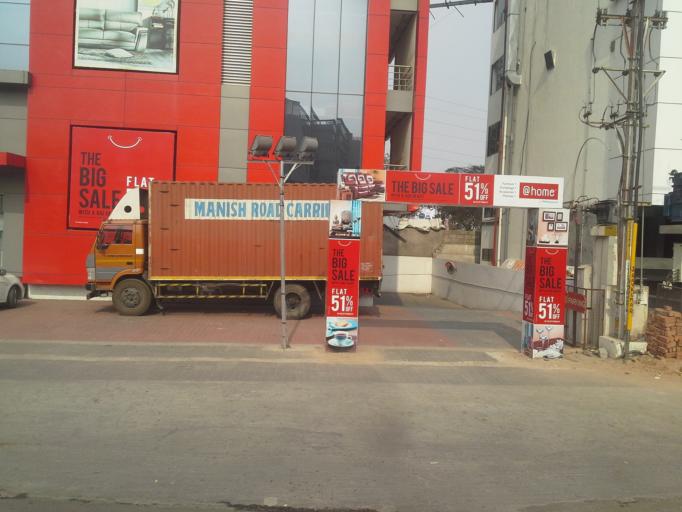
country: IN
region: Telangana
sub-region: Rangareddi
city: Kukatpalli
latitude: 17.4521
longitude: 78.3808
